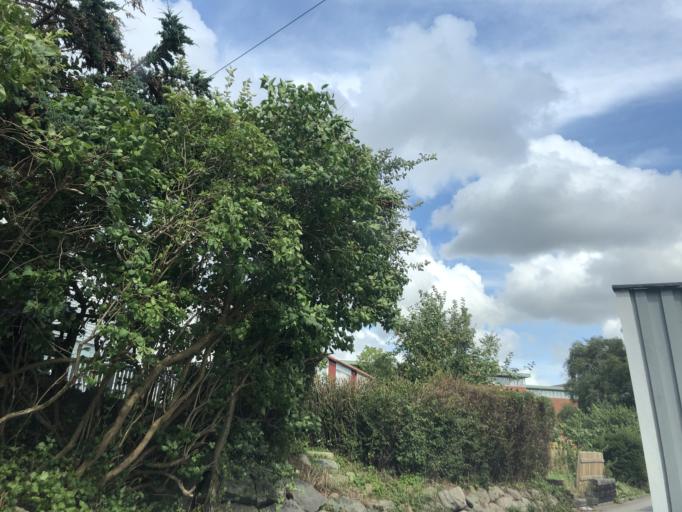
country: SE
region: Vaestra Goetaland
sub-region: Goteborg
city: Majorna
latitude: 57.7131
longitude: 11.8863
